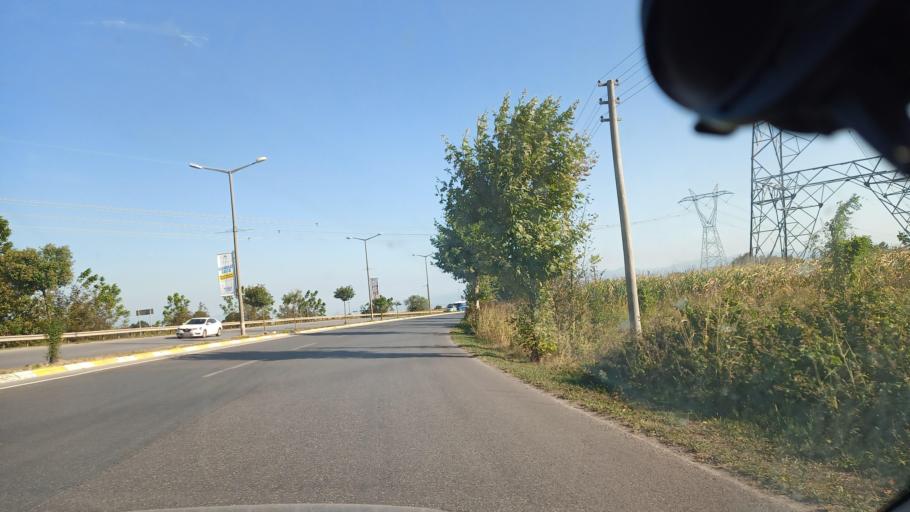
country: TR
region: Sakarya
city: Kazimpasa
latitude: 40.8383
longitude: 30.3441
